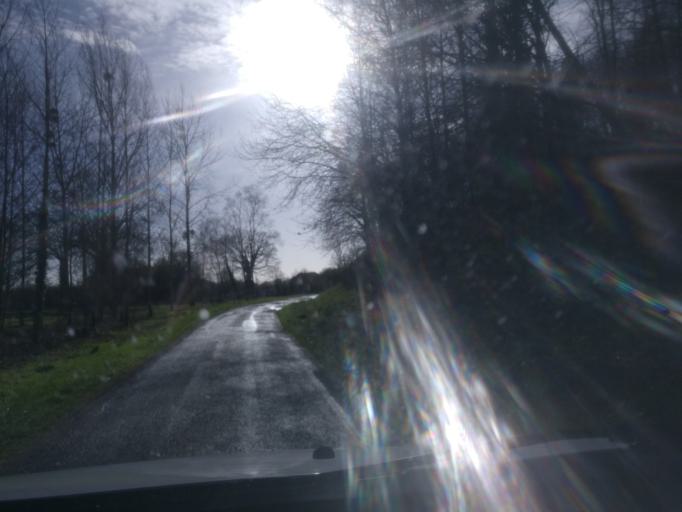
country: FR
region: Brittany
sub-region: Departement d'Ille-et-Vilaine
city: Antrain
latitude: 48.4995
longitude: -1.4996
